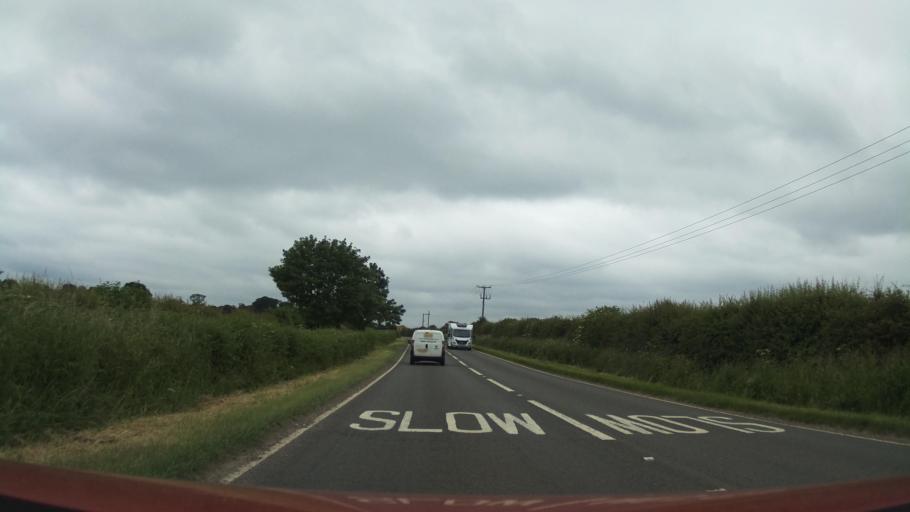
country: GB
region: England
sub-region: Nottinghamshire
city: East Leake
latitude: 52.8152
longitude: -1.1631
